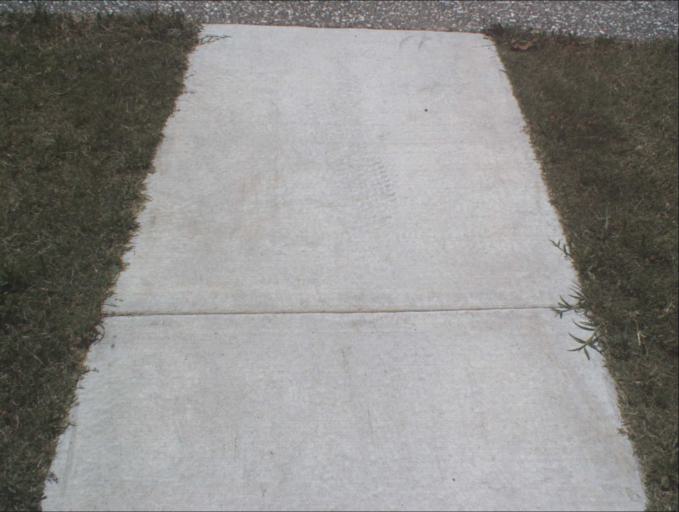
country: AU
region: Queensland
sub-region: Logan
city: Rochedale South
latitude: -27.5981
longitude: 153.1075
